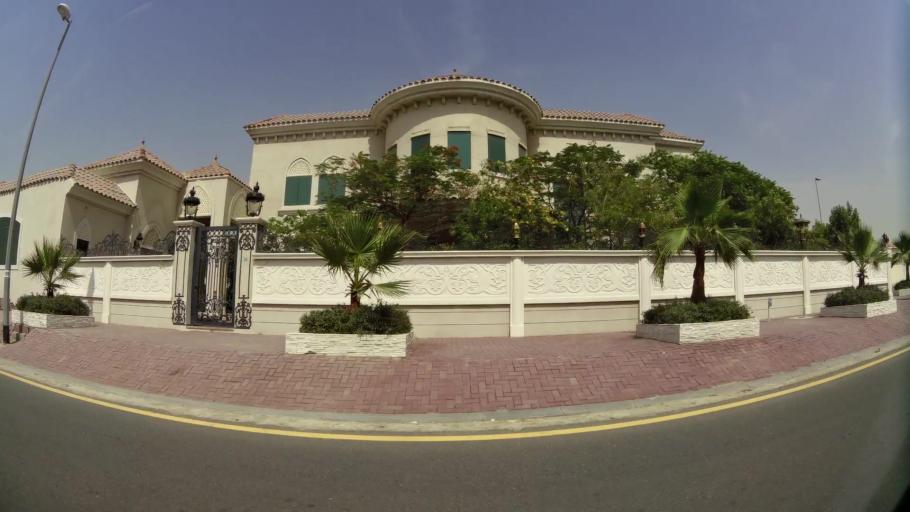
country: AE
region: Ash Shariqah
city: Sharjah
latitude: 25.2451
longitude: 55.4915
